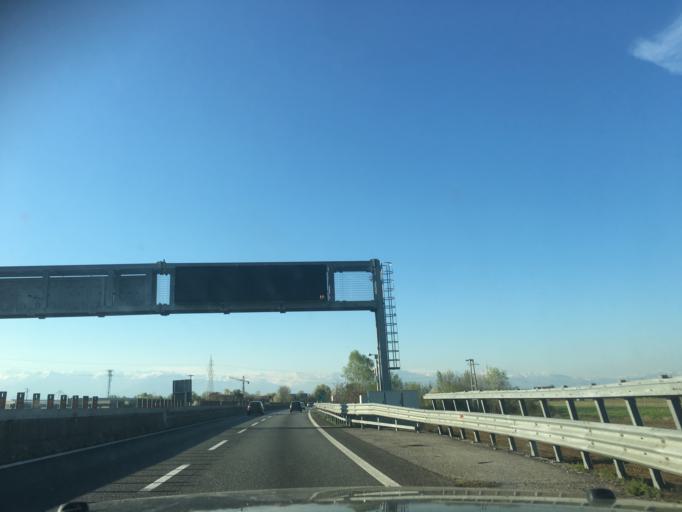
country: IT
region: Piedmont
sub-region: Provincia di Torino
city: Borgaro Torinese
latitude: 45.1456
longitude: 7.6888
